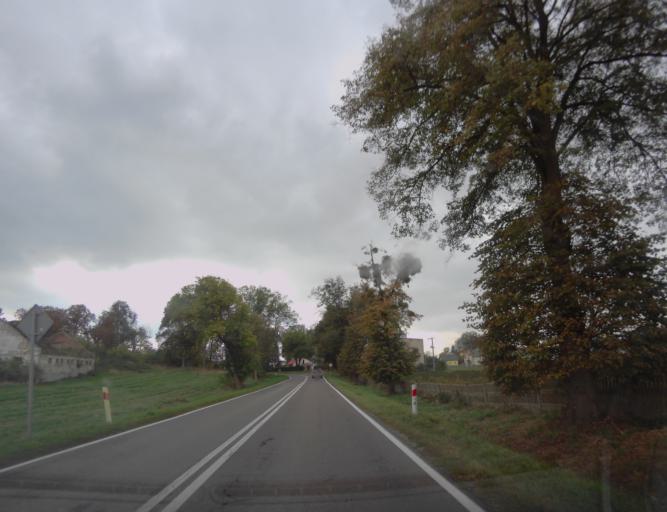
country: PL
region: Lublin Voivodeship
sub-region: Powiat krasnostawski
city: Zolkiewka
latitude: 50.9190
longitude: 22.8557
